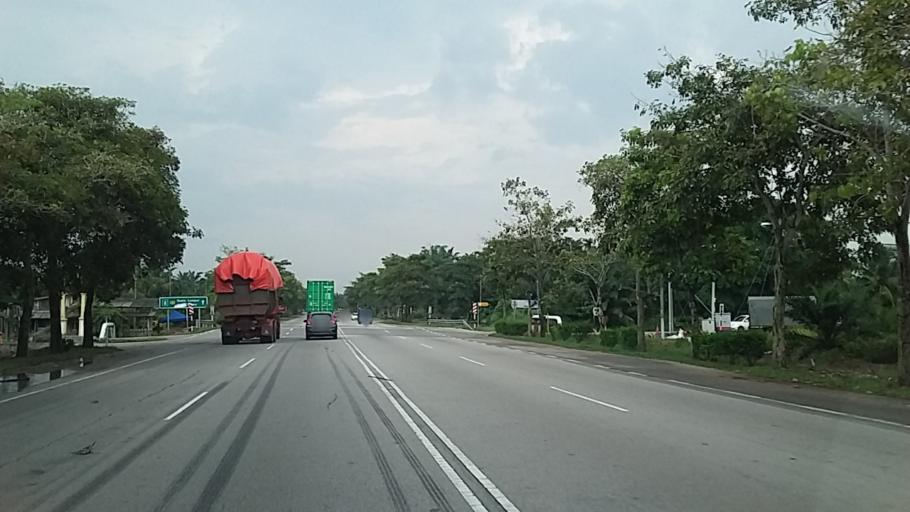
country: MY
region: Johor
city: Parit Raja
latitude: 1.8738
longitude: 103.1372
